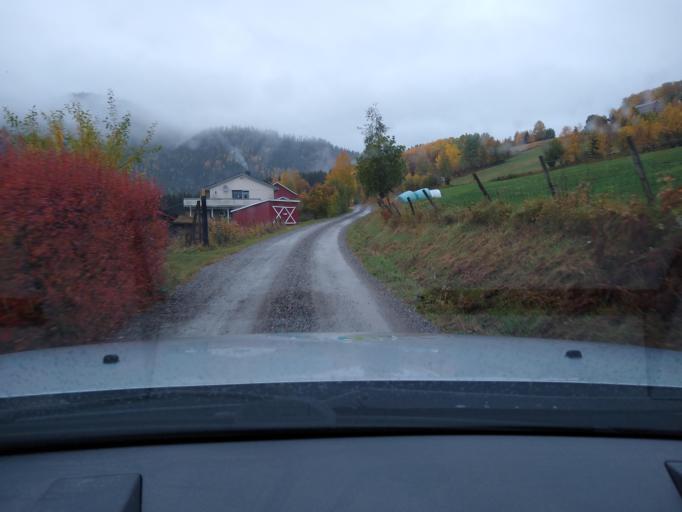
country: NO
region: Oppland
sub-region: Ringebu
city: Ringebu
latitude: 61.5470
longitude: 10.1496
